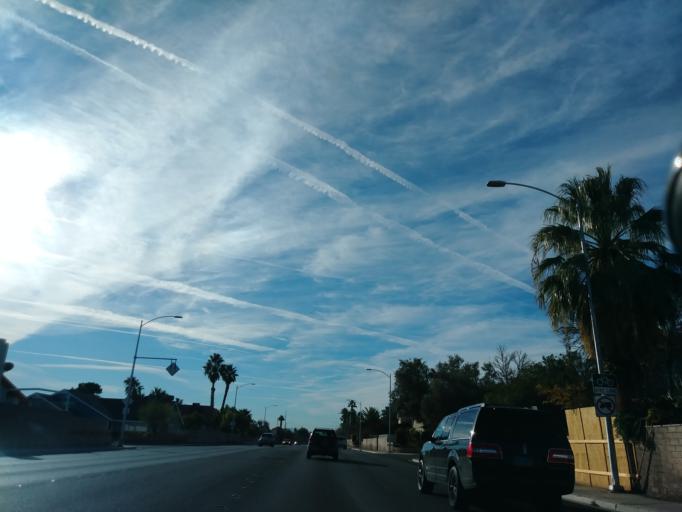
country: US
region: Nevada
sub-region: Clark County
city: Spring Valley
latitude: 36.1477
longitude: -115.2342
